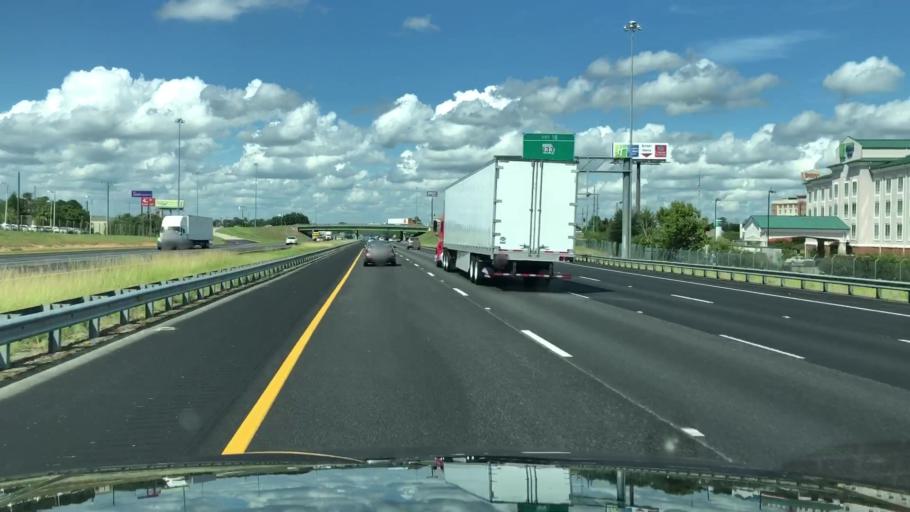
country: US
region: Georgia
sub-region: Lowndes County
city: Remerton
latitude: 30.8413
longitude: -83.3290
